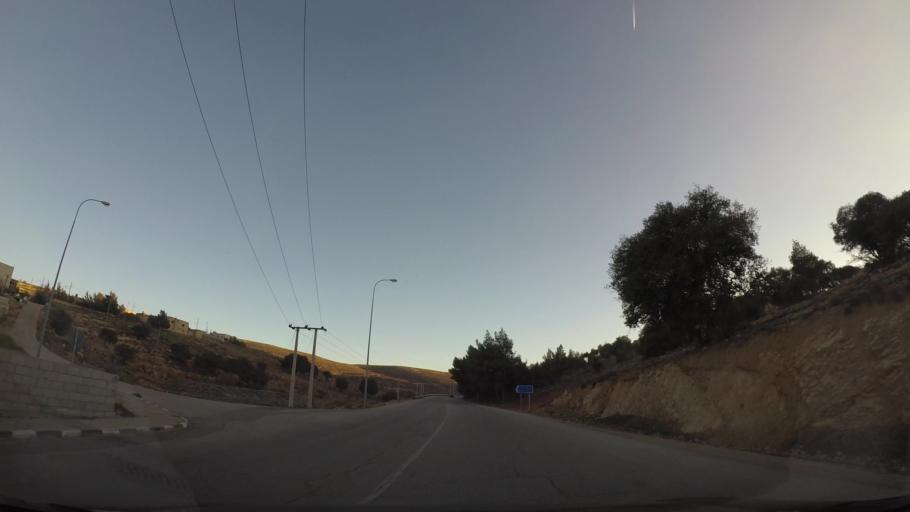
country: JO
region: Ma'an
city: Petra
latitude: 30.4145
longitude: 35.5080
